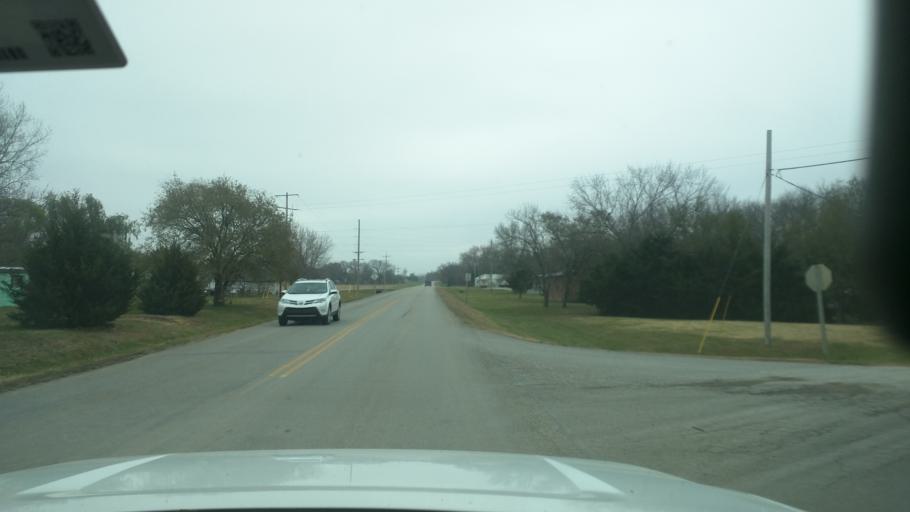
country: US
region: Kansas
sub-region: Lyon County
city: Emporia
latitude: 38.5033
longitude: -96.2607
